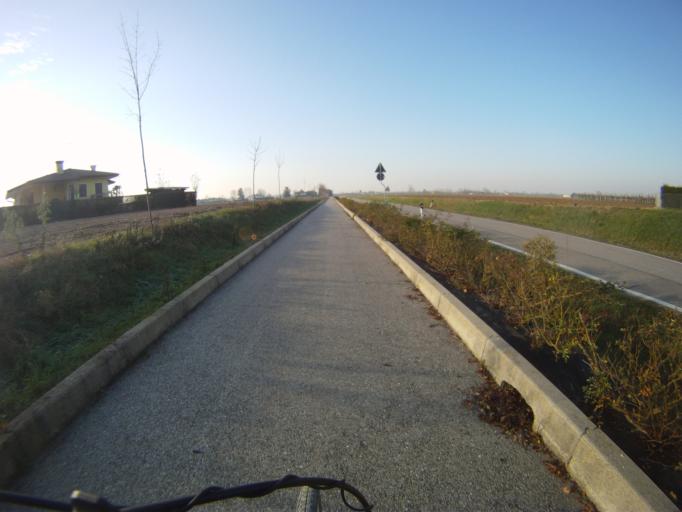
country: IT
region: Veneto
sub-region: Provincia di Padova
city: Polverara
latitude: 45.3186
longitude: 11.9533
